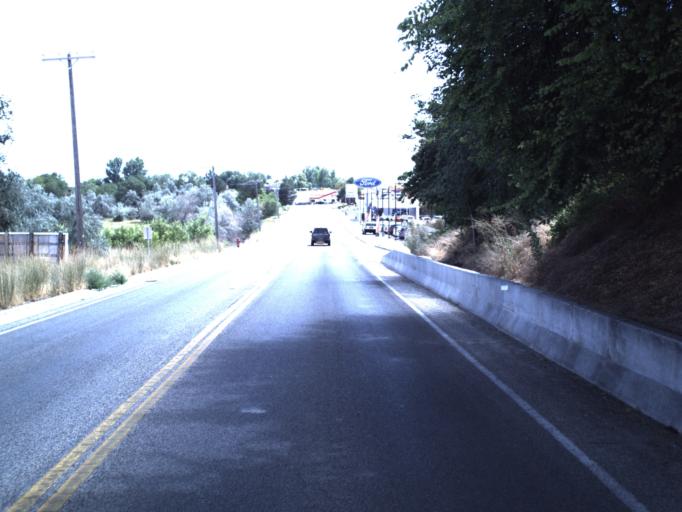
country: US
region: Utah
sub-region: Box Elder County
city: Tremonton
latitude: 41.7153
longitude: -112.1619
